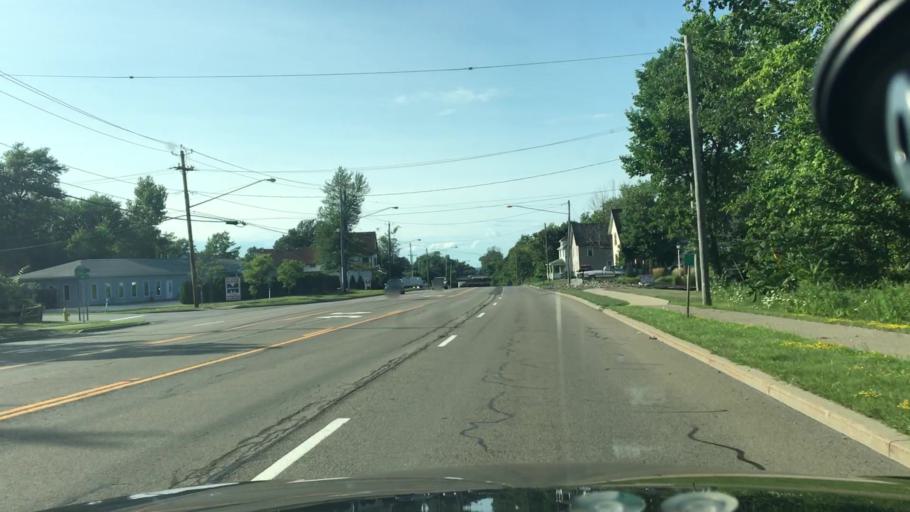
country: US
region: New York
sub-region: Erie County
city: Wanakah
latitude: 42.7614
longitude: -78.8624
